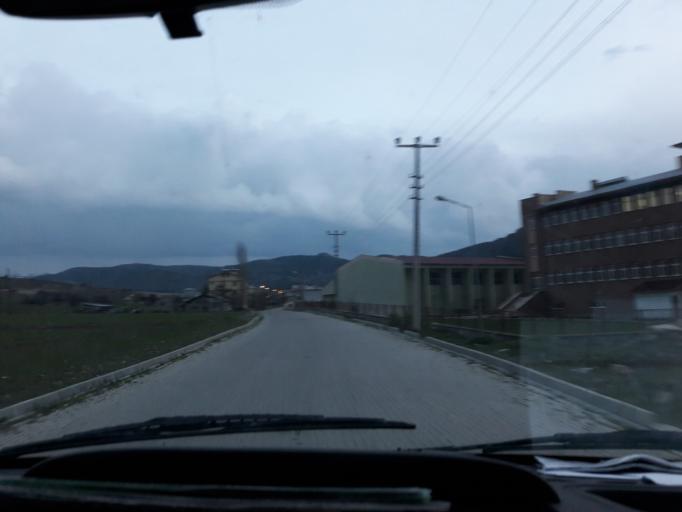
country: TR
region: Giresun
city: Alucra
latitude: 40.3243
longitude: 38.7709
